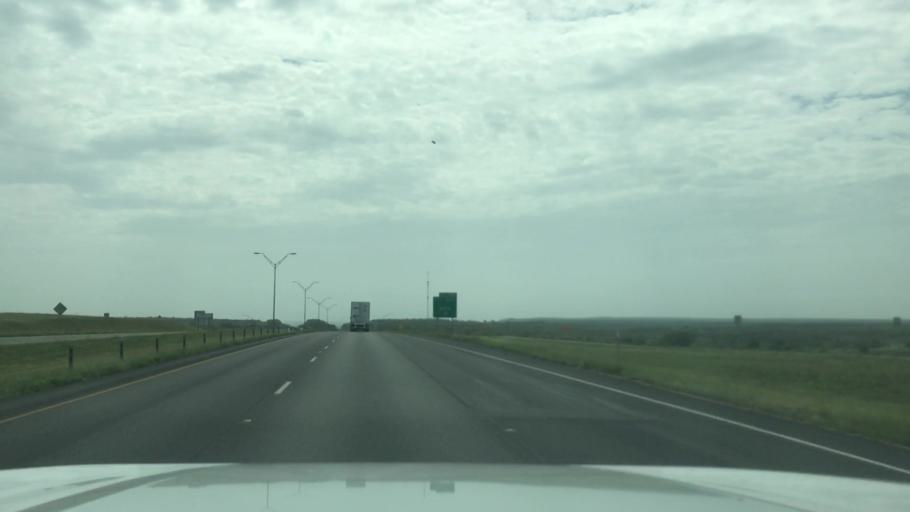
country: US
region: Texas
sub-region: Callahan County
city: Baird
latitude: 32.3999
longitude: -99.3794
